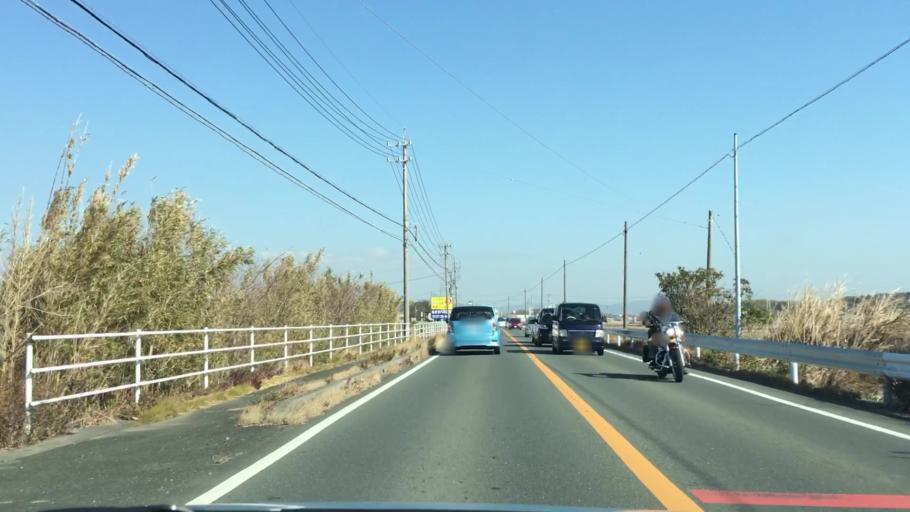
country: JP
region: Aichi
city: Tahara
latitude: 34.6778
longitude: 137.3104
